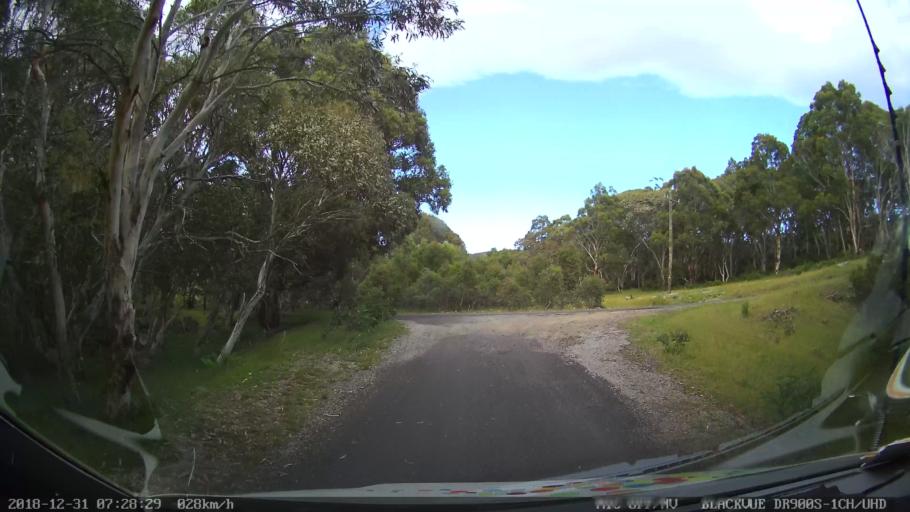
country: AU
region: New South Wales
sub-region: Snowy River
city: Jindabyne
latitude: -36.3222
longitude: 148.4750
